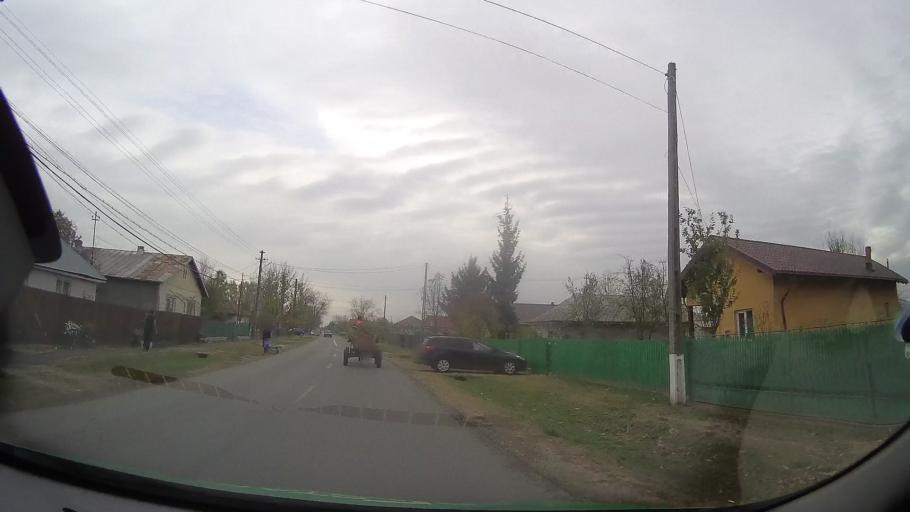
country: RO
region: Prahova
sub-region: Comuna Valea Calugareasca
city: Pantazi
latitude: 44.9171
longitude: 26.1564
